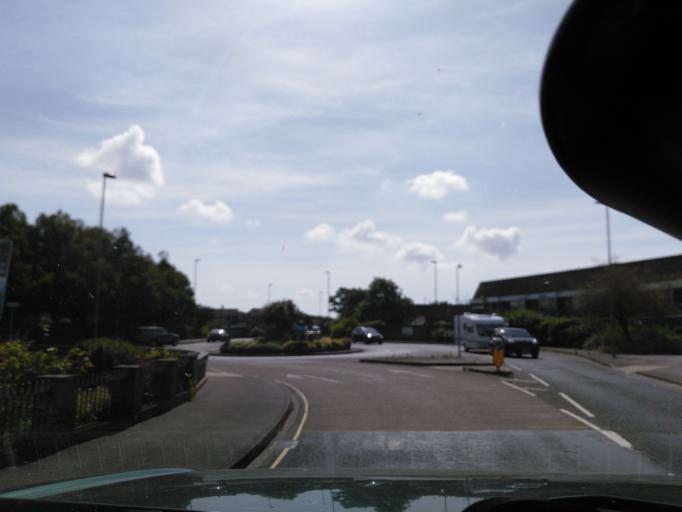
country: GB
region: England
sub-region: Hampshire
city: Lee-on-the-Solent
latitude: 50.8268
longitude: -1.2146
